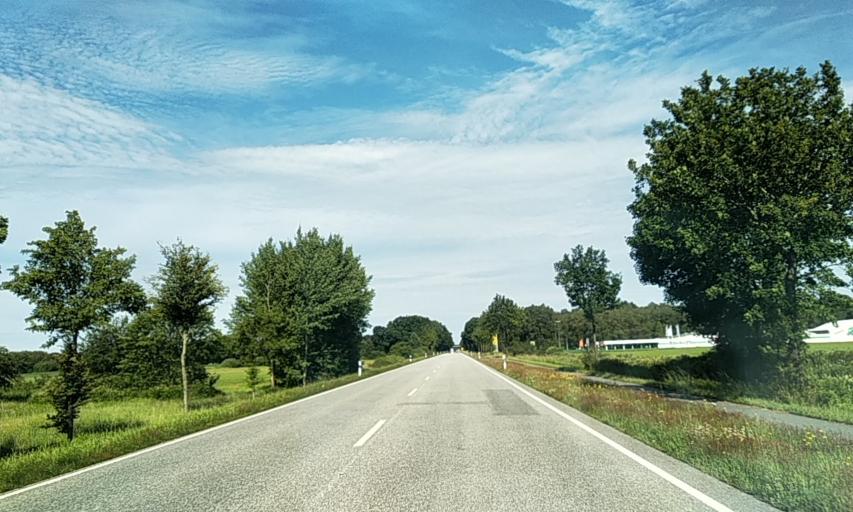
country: DE
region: Schleswig-Holstein
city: Owschlag
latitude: 54.3418
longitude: 9.5982
